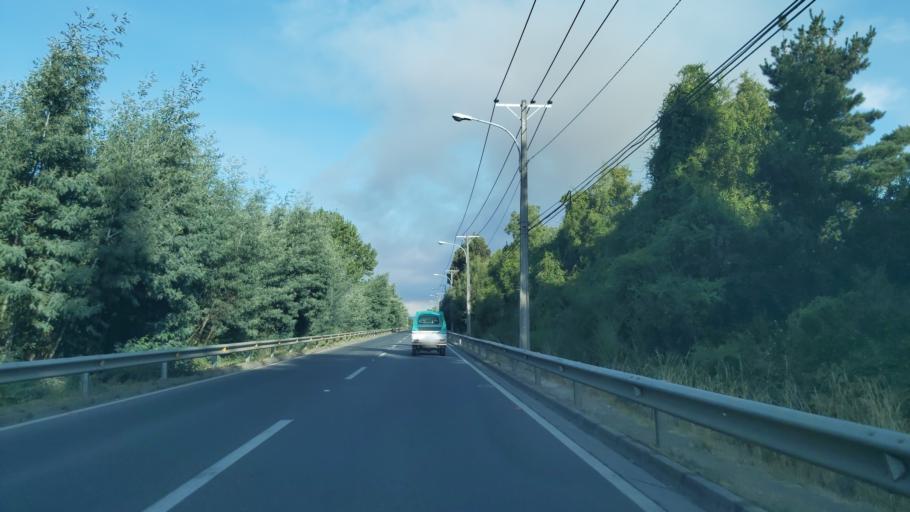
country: CL
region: Biobio
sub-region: Provincia de Concepcion
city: Chiguayante
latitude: -36.9657
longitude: -73.0027
